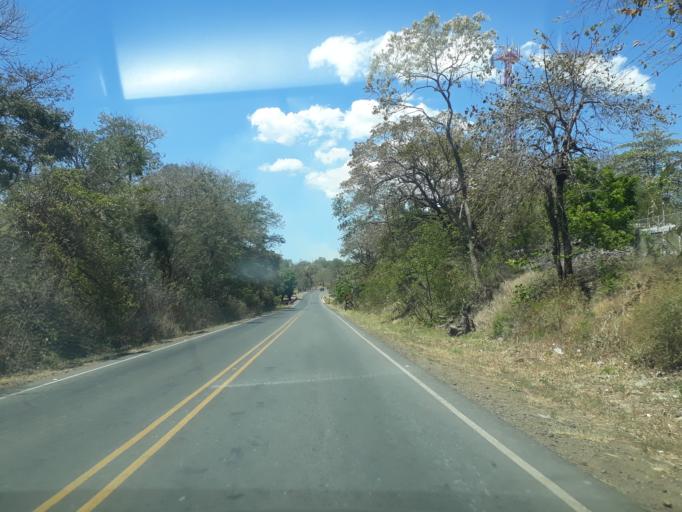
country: CR
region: Guanacaste
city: Liberia
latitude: 10.6683
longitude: -85.4795
